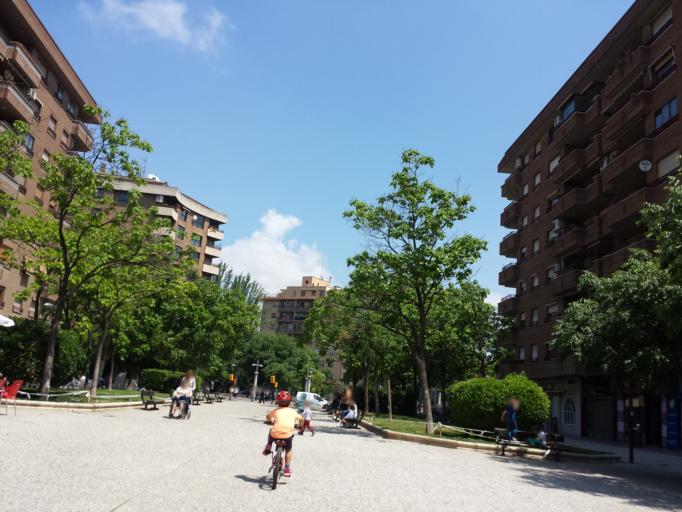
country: ES
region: Aragon
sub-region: Provincia de Zaragoza
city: Almozara
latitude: 41.6592
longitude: -0.8956
